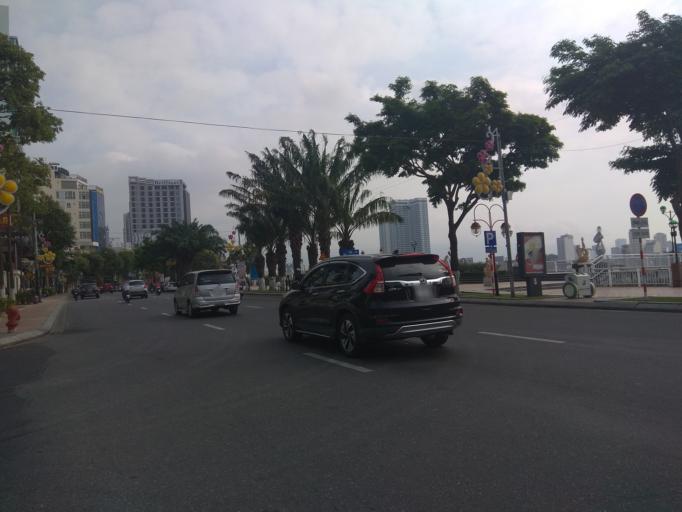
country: VN
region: Da Nang
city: Da Nang
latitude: 16.0637
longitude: 108.2241
